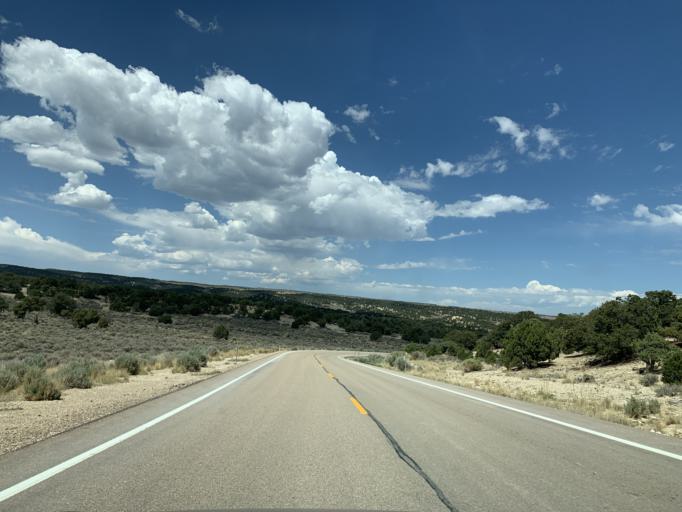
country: US
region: Utah
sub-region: Duchesne County
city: Duchesne
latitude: 39.8862
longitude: -110.2346
